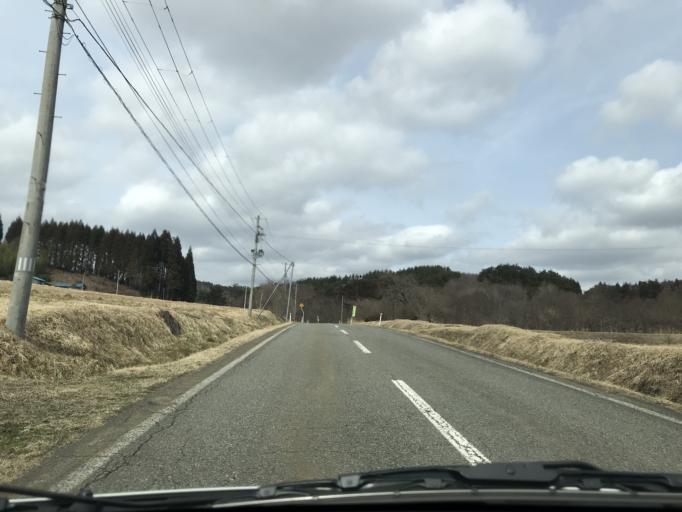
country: JP
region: Iwate
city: Kitakami
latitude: 39.2536
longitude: 141.3176
